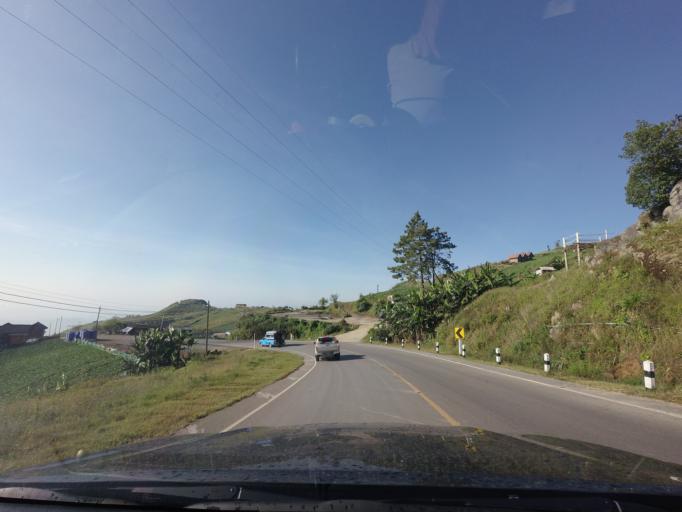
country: TH
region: Phetchabun
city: Lom Kao
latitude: 16.8910
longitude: 101.0969
